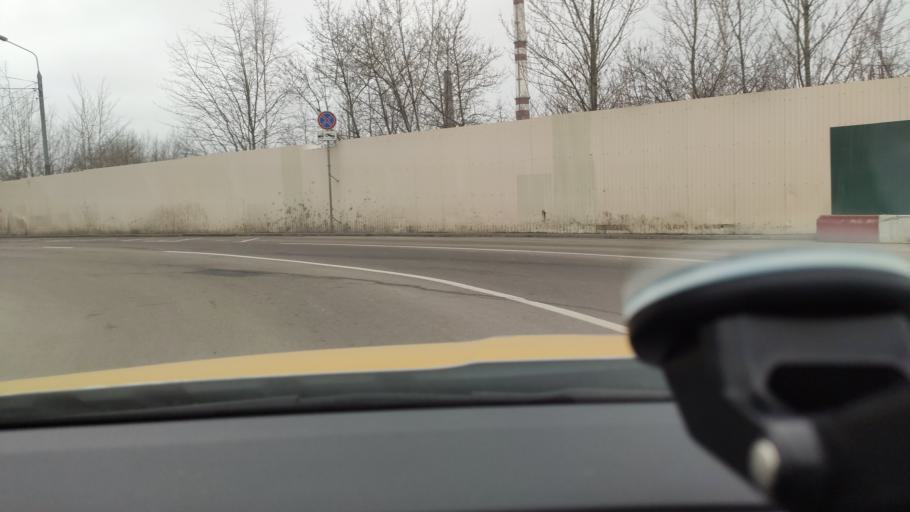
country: RU
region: Moskovskaya
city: Kozhukhovo
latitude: 55.6965
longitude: 37.6629
